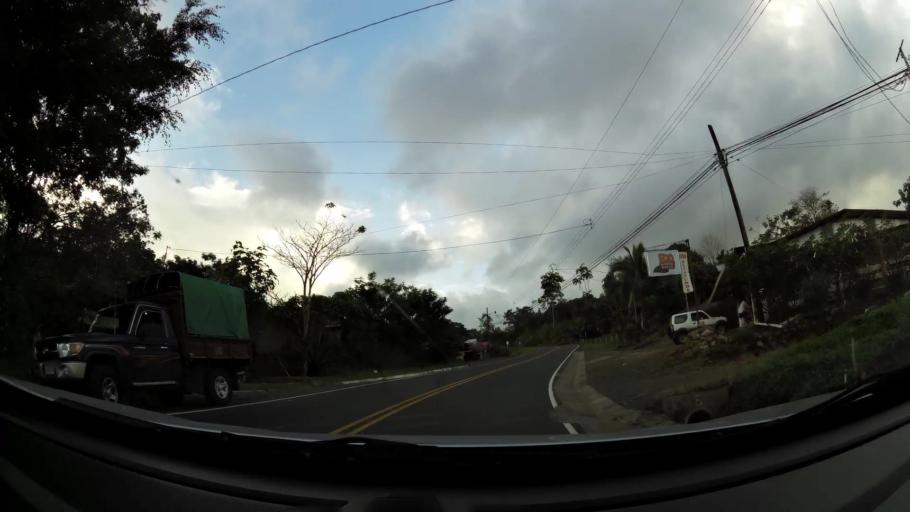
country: CR
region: Limon
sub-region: Canton de Siquirres
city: Siquirres
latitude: 9.9846
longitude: -83.5704
